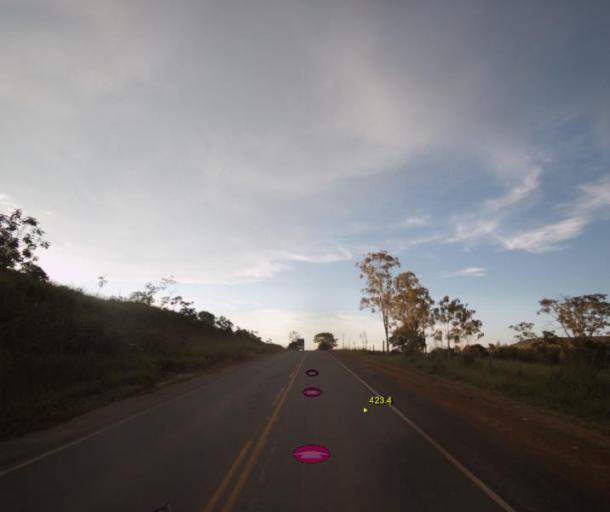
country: BR
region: Goias
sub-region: Anapolis
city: Anapolis
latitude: -16.1539
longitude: -48.8888
